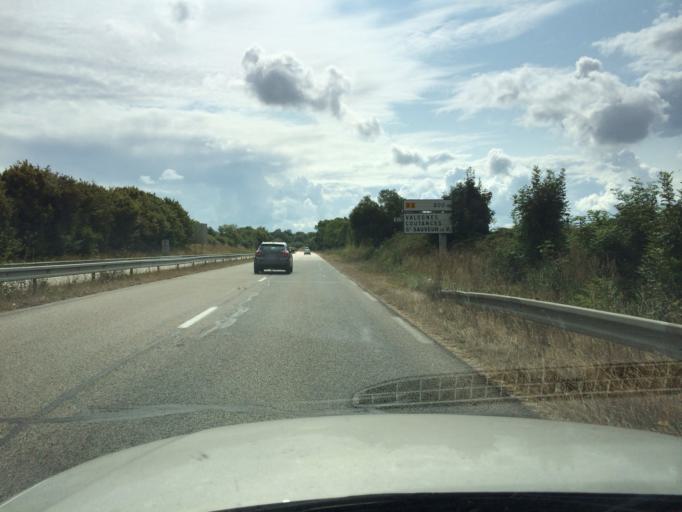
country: FR
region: Lower Normandy
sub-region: Departement de la Manche
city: Valognes
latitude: 49.4984
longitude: -1.4809
